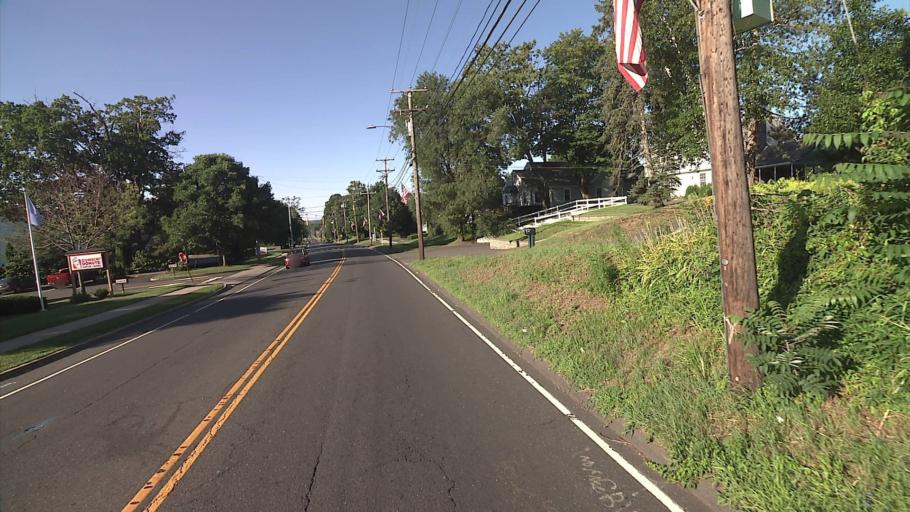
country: US
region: Connecticut
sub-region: New Haven County
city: Cheshire
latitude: 41.4945
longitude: -72.9036
